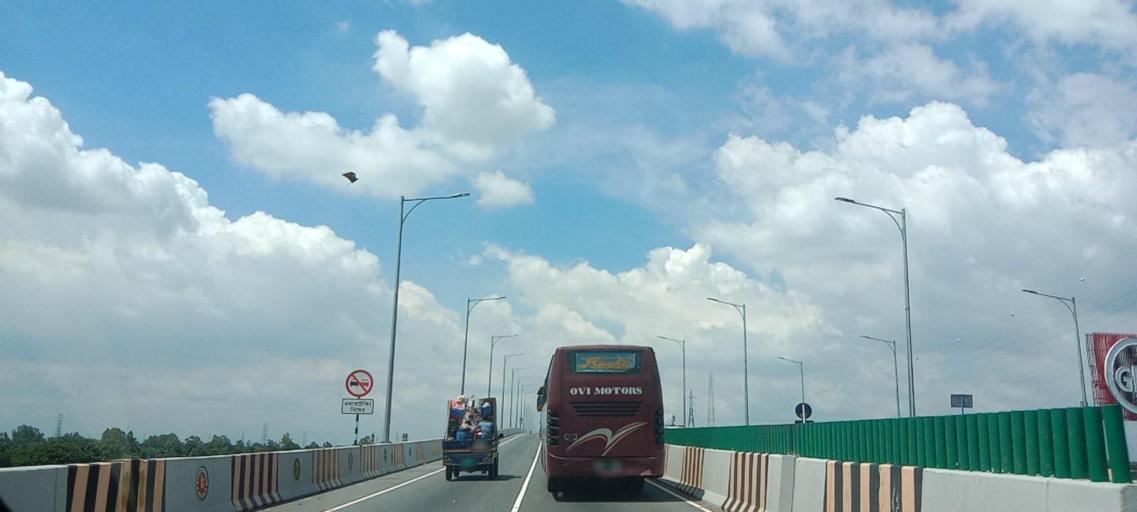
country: BD
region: Dhaka
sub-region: Dhaka
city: Dhaka
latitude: 23.6345
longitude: 90.3451
